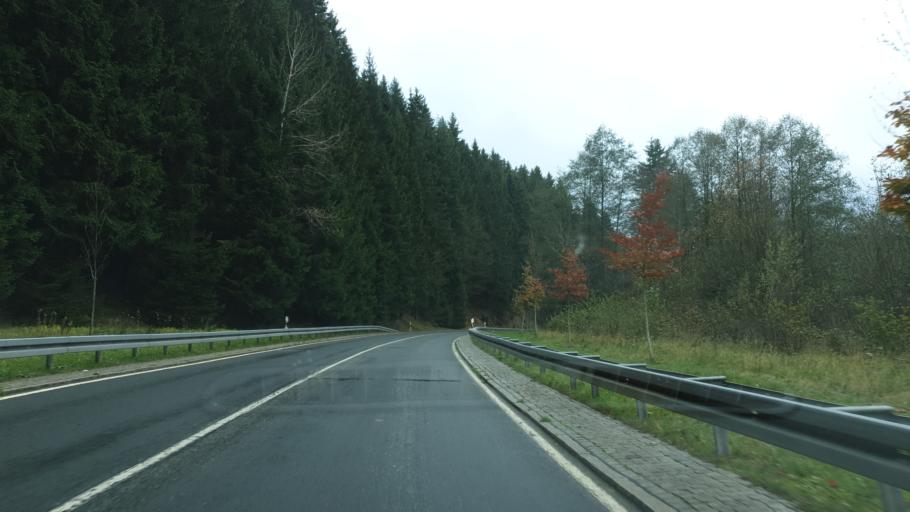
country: DE
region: Saxony
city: Schoenheide
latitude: 50.4973
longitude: 12.5504
